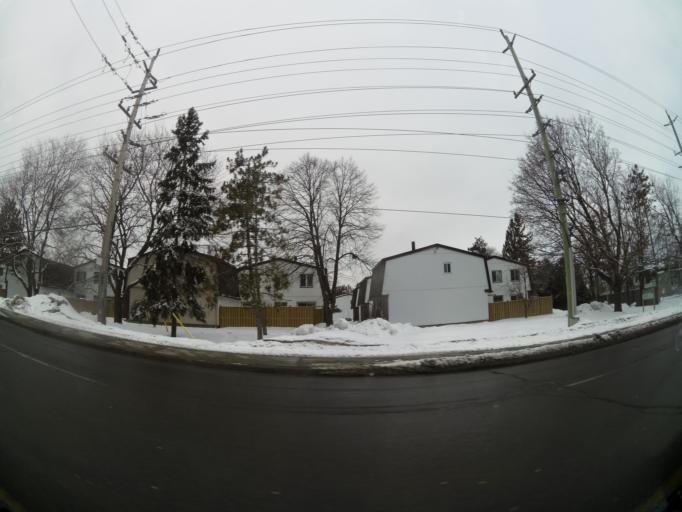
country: CA
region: Quebec
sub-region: Outaouais
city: Gatineau
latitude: 45.4517
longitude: -75.5891
